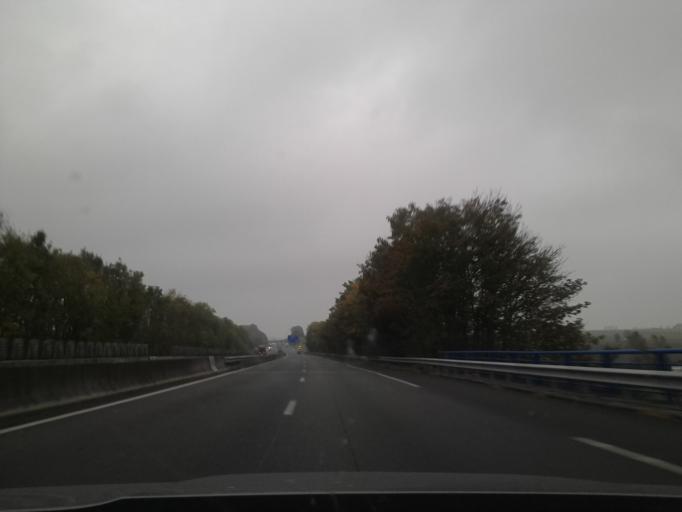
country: FR
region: Nord-Pas-de-Calais
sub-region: Departement du Nord
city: Raillencourt-Sainte-Olle
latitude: 50.1849
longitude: 3.1912
